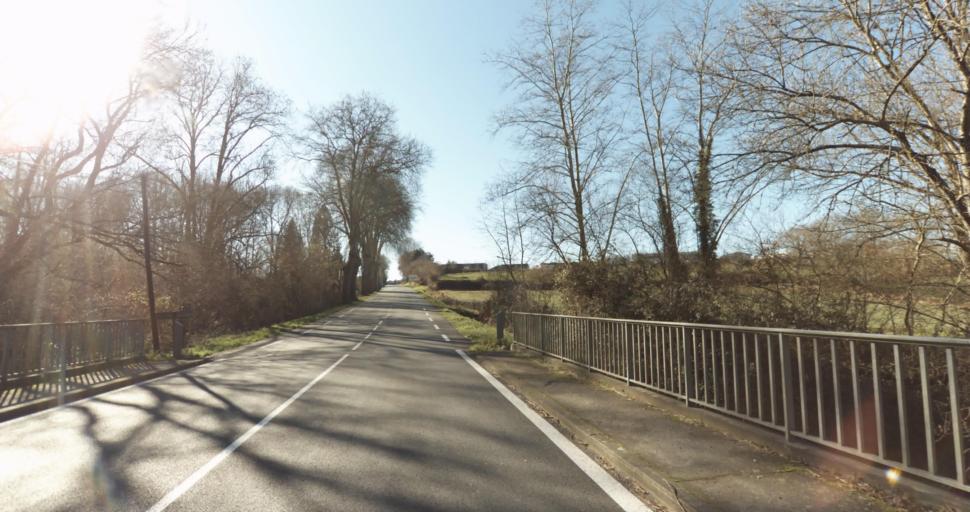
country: FR
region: Aquitaine
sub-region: Departement des Pyrenees-Atlantiques
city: Morlaas
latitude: 43.3541
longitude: -0.2532
